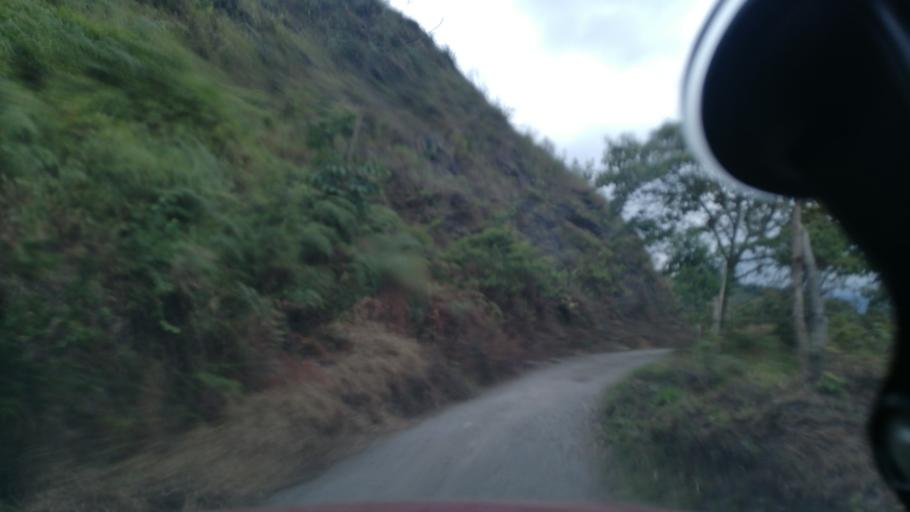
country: CO
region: Cundinamarca
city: Vergara
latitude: 5.1751
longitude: -74.2690
